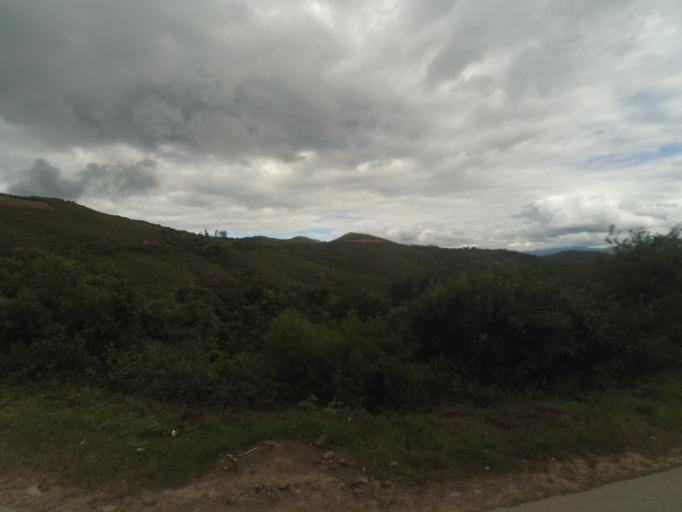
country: BO
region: Santa Cruz
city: Samaipata
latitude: -18.1752
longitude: -63.8726
